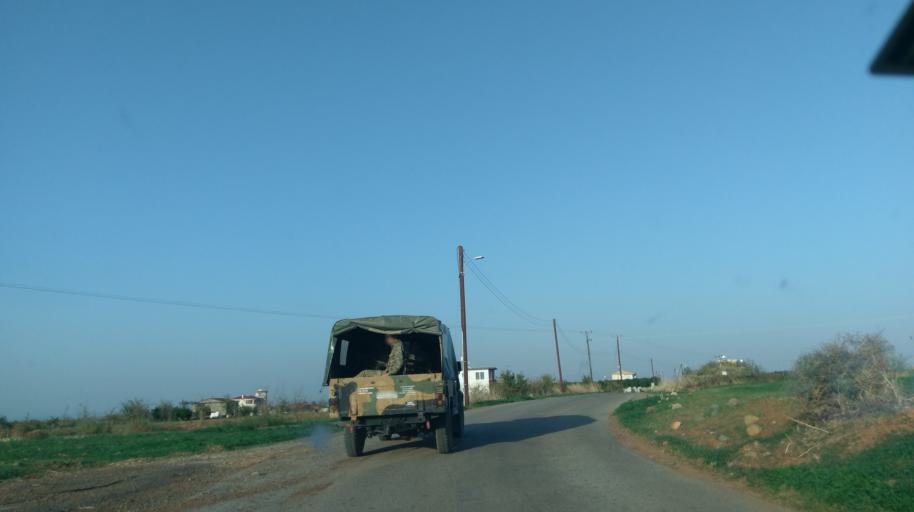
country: CY
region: Lefkosia
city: Morfou
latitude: 35.1233
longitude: 32.9512
